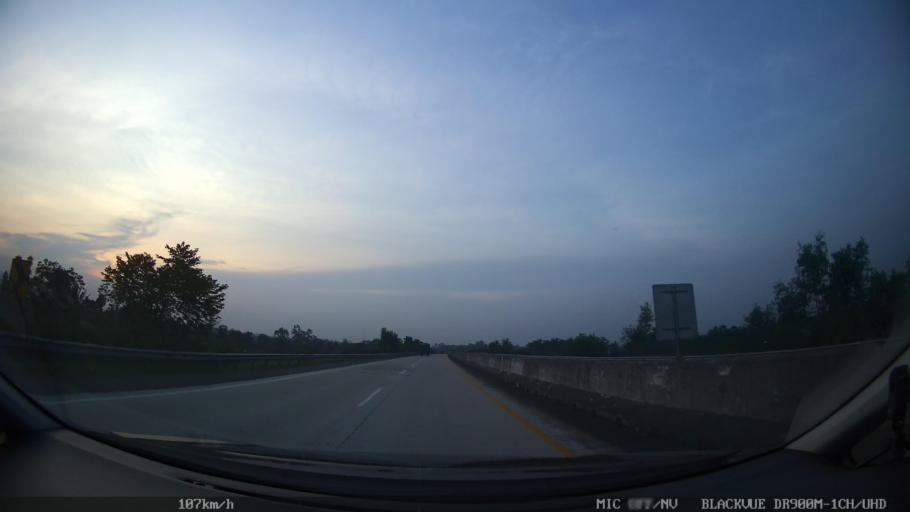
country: ID
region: Lampung
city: Pasuruan
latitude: -5.7403
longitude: 105.6926
